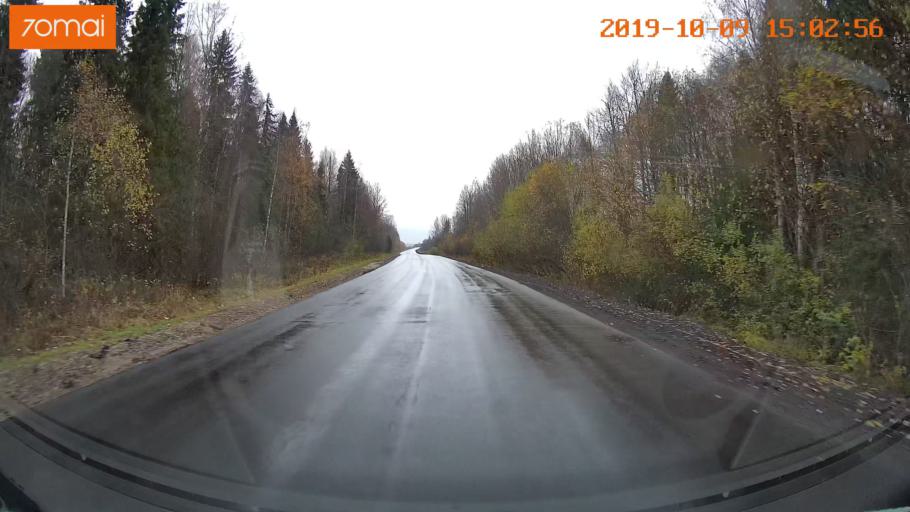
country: RU
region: Kostroma
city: Chistyye Bory
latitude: 58.2782
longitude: 41.6766
